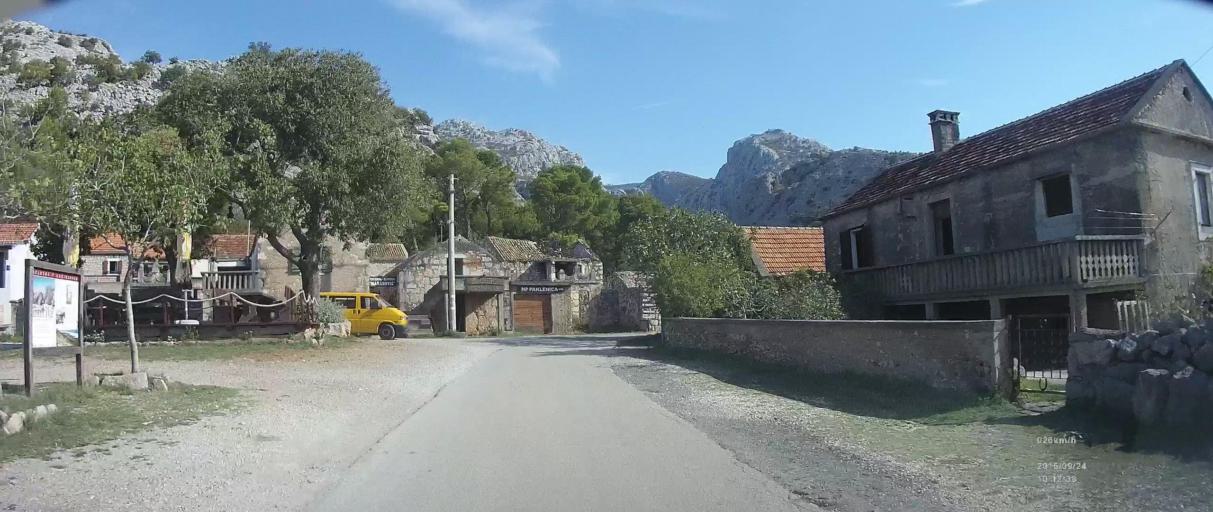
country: HR
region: Zadarska
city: Starigrad
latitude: 44.2922
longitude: 15.4552
